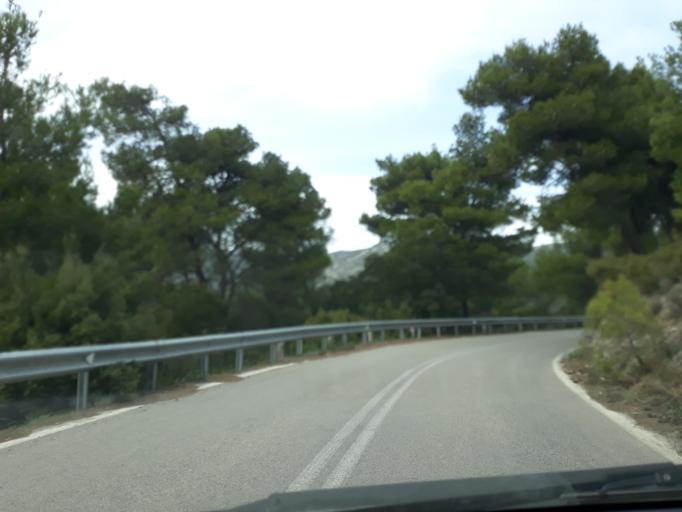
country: GR
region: Attica
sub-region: Nomarchia Anatolikis Attikis
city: Varybobi
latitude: 38.1482
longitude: 23.7910
